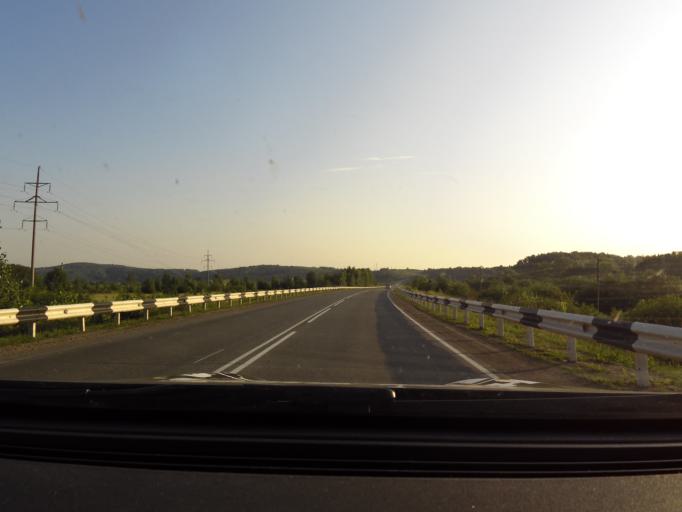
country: RU
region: Sverdlovsk
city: Mikhaylovsk
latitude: 56.4302
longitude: 59.0797
